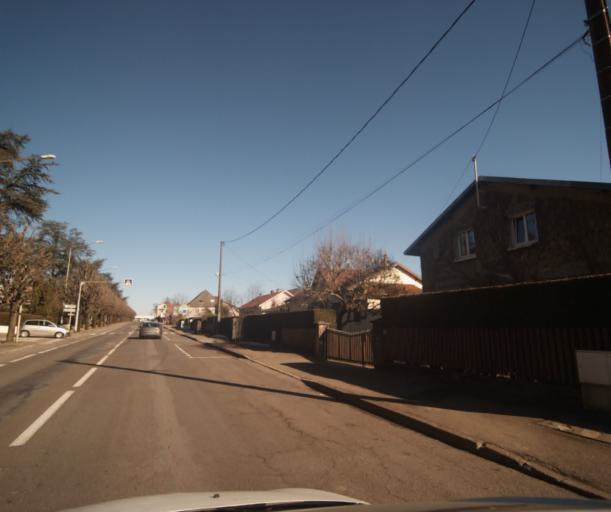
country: FR
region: Franche-Comte
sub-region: Departement du Doubs
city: Besancon
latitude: 47.2596
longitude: 6.0463
